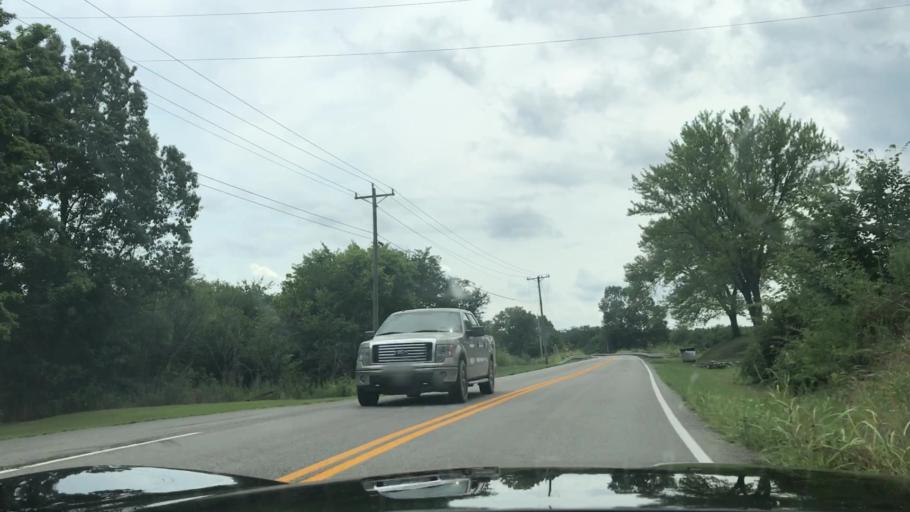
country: US
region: Kentucky
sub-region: Ohio County
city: Beaver Dam
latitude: 37.2131
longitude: -86.9017
